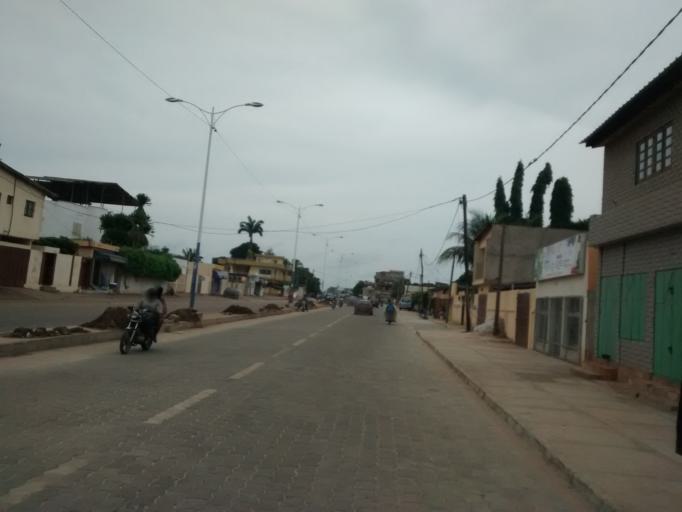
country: TG
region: Maritime
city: Lome
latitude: 6.1734
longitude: 1.1986
